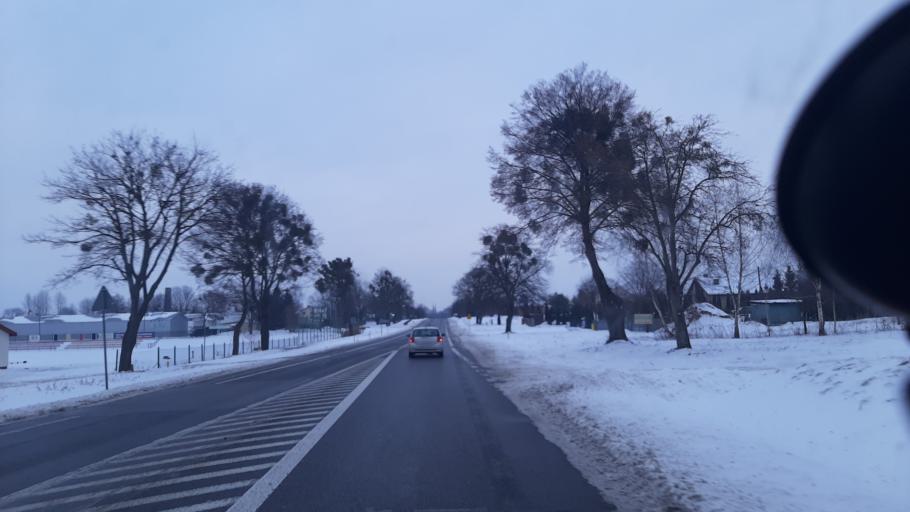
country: PL
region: Lublin Voivodeship
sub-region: Powiat lubelski
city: Garbow
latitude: 51.3589
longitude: 22.3164
